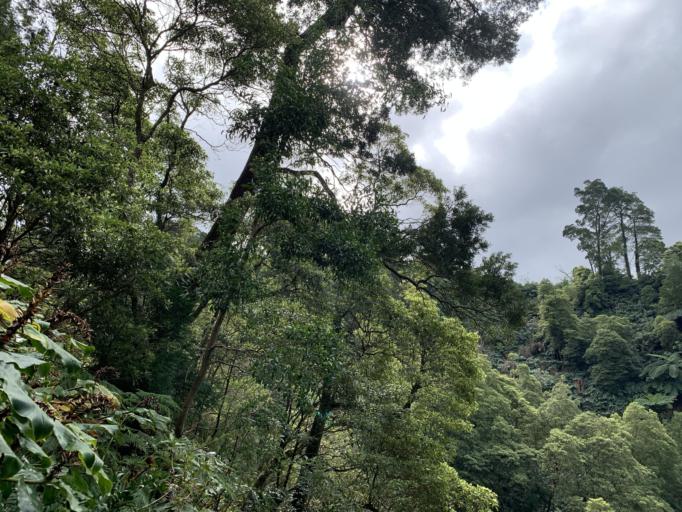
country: PT
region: Azores
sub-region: Ribeira Grande
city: Rabo de Peixe
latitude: 37.7948
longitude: -25.4912
